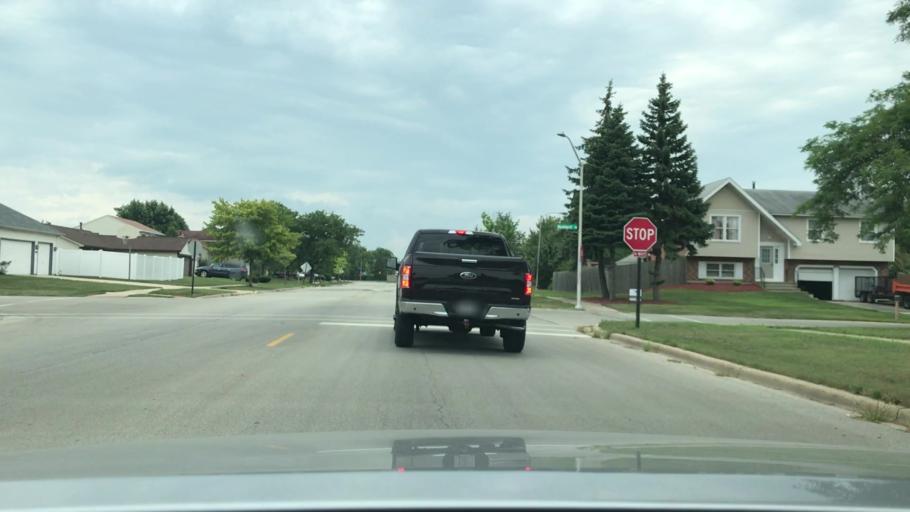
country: US
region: Illinois
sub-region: Will County
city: Bolingbrook
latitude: 41.7067
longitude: -88.0393
